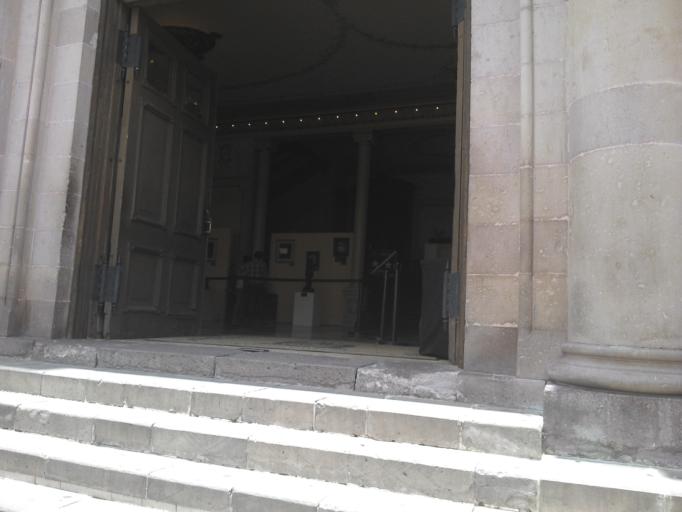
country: MX
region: Zacatecas
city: Zacatecas
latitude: 22.7751
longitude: -102.5731
